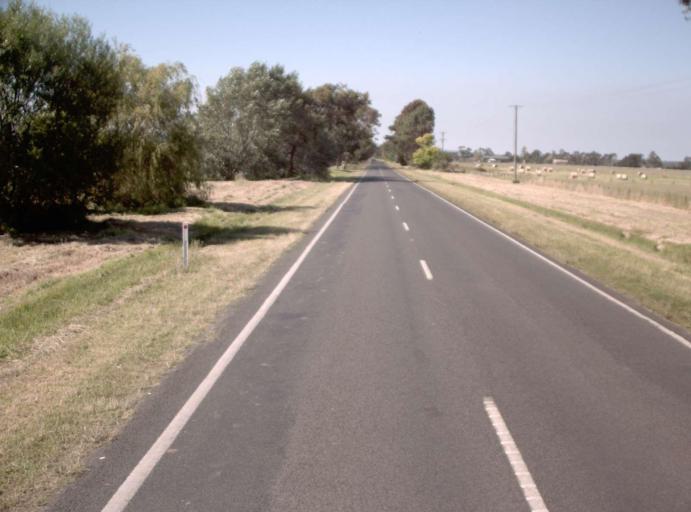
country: AU
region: Victoria
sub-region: Latrobe
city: Traralgon
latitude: -38.5885
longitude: 146.6704
